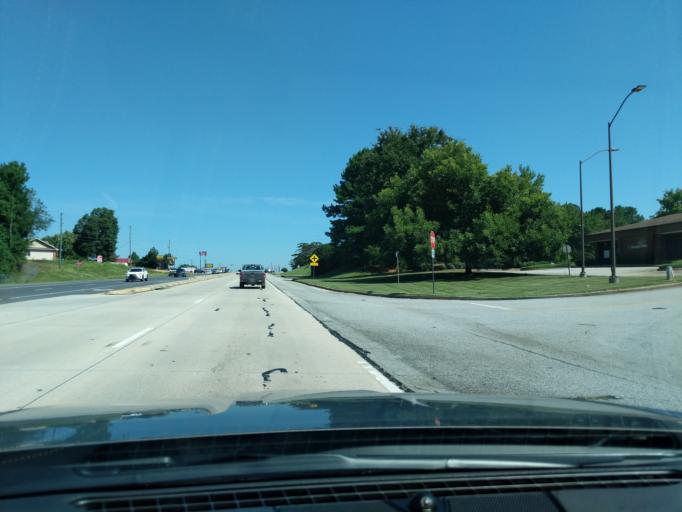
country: US
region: Georgia
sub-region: Habersham County
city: Baldwin
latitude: 34.5066
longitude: -83.5452
